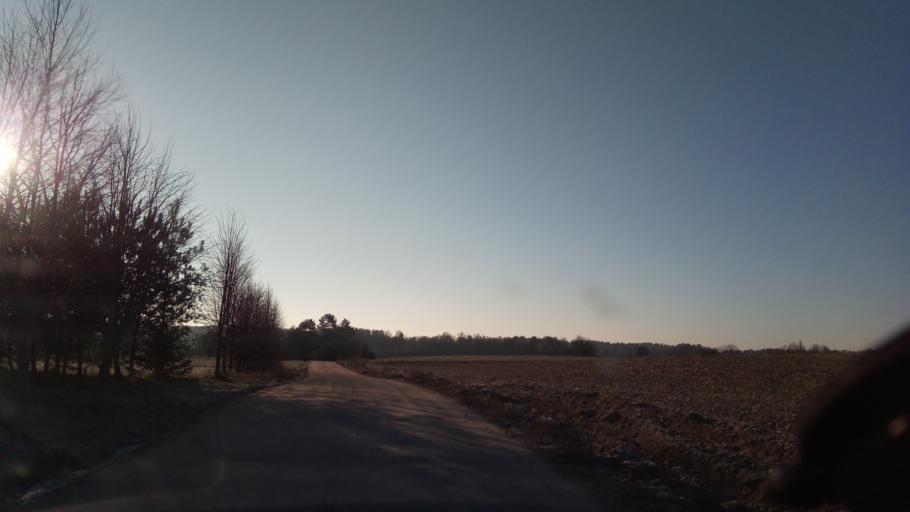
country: LT
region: Alytaus apskritis
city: Druskininkai
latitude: 54.1095
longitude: 24.0128
